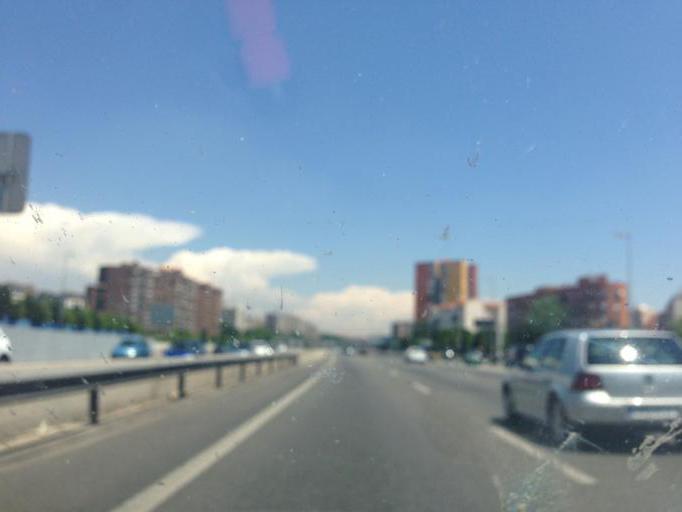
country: ES
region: Madrid
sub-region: Provincia de Madrid
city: Puente de Vallecas
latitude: 40.4007
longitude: -3.6678
